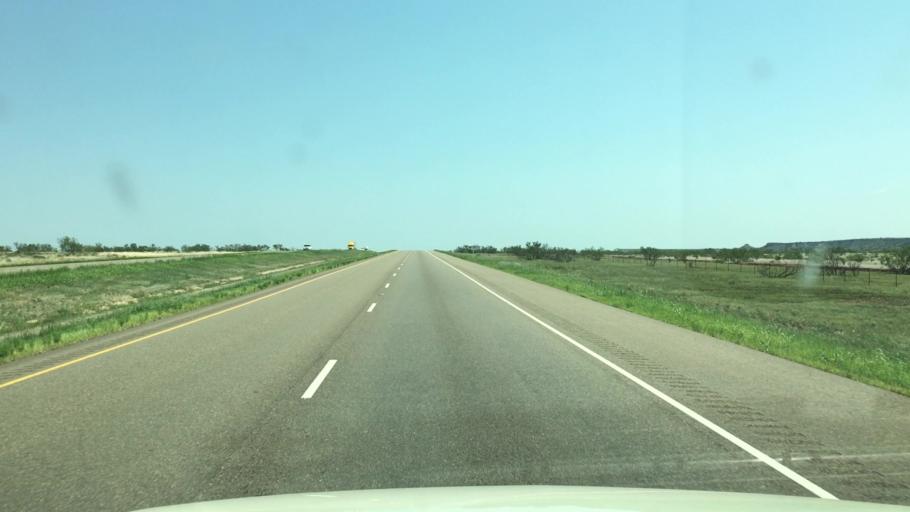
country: US
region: Texas
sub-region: Oldham County
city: Vega
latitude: 35.2241
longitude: -102.8759
